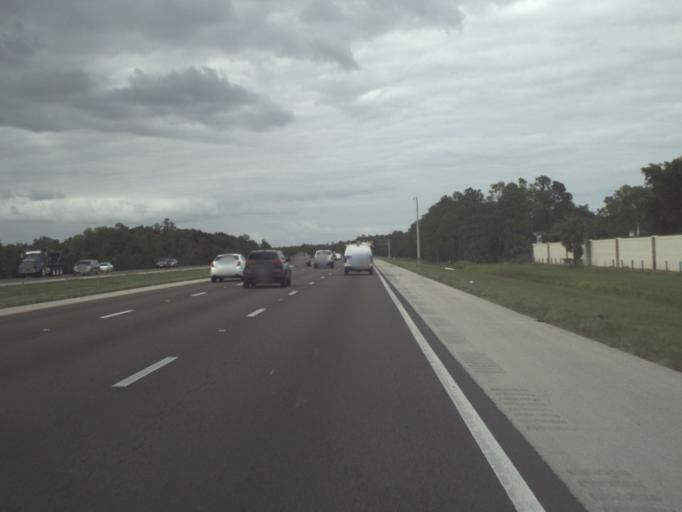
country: US
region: Florida
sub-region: Lee County
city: Bonita Springs
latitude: 26.3007
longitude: -81.7427
